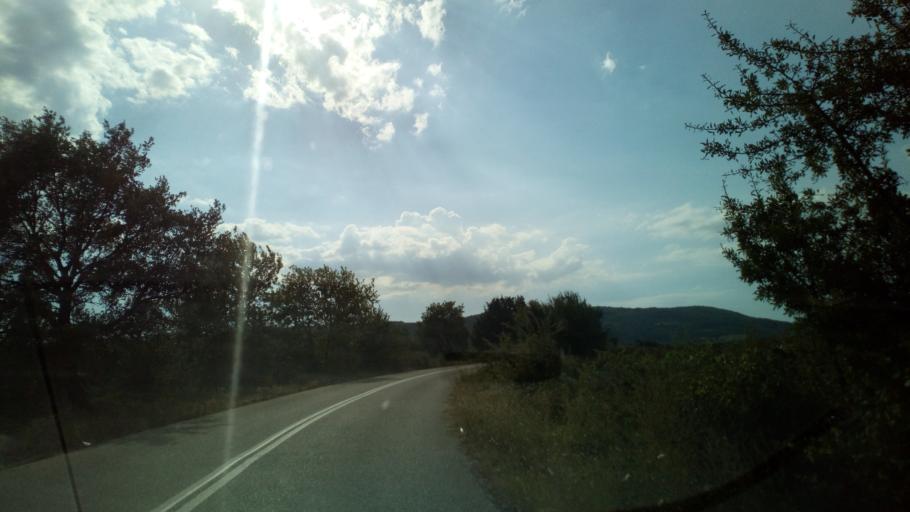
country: GR
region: Central Macedonia
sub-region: Nomos Chalkidikis
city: Galatista
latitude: 40.5269
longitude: 23.3419
